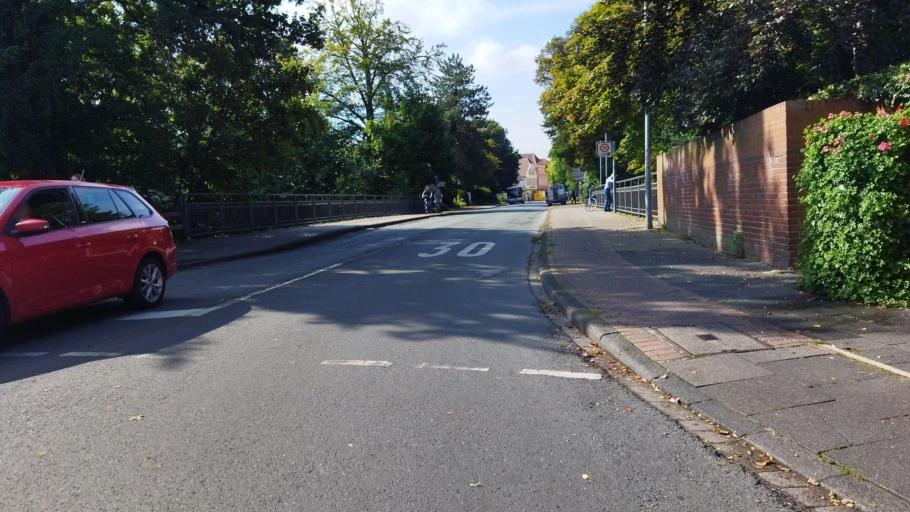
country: DE
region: North Rhine-Westphalia
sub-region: Regierungsbezirk Munster
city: Warendorf
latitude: 51.9552
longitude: 7.9929
